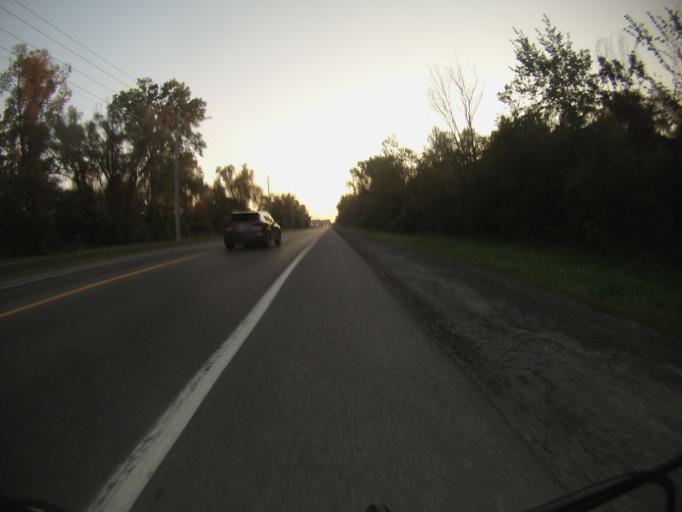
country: CA
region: Ontario
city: Ottawa
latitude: 45.3647
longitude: -75.6461
